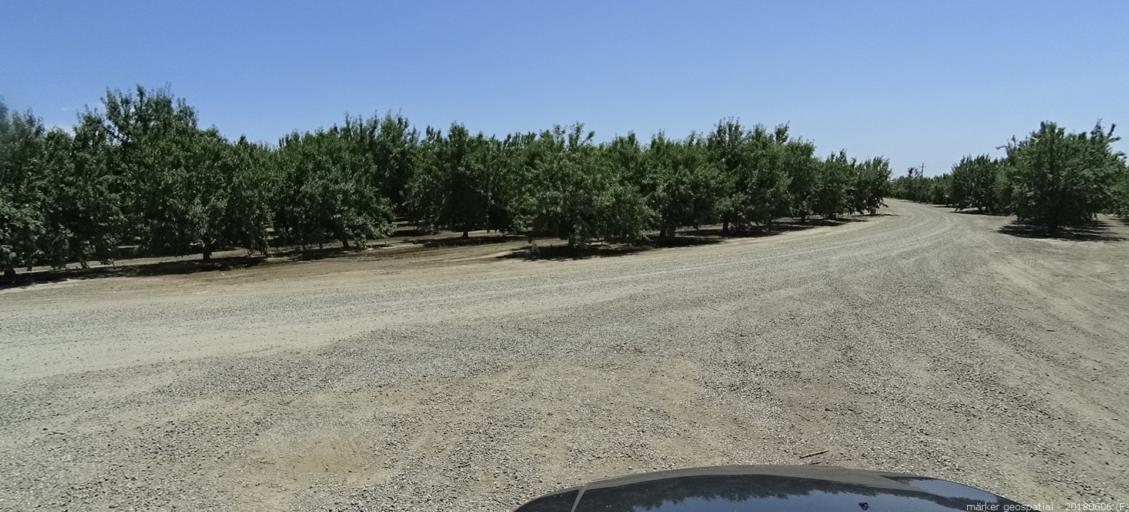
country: US
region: California
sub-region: Fresno County
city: Mendota
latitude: 36.8032
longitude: -120.3509
